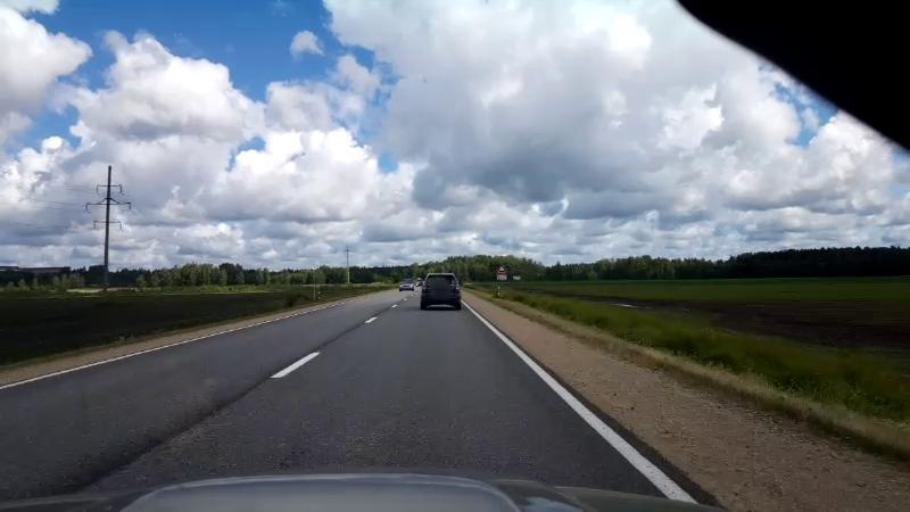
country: LV
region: Salaspils
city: Salaspils
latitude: 56.8604
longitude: 24.4043
